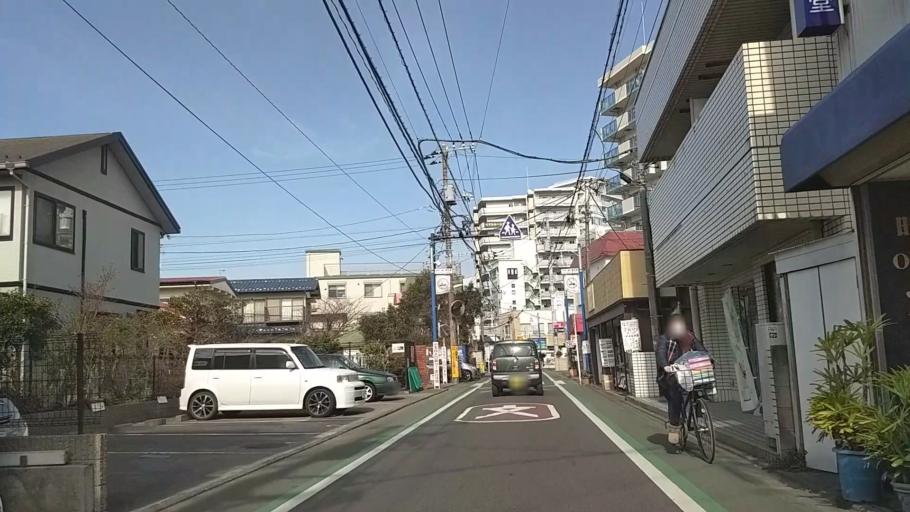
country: JP
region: Kanagawa
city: Chigasaki
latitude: 35.3277
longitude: 139.4040
